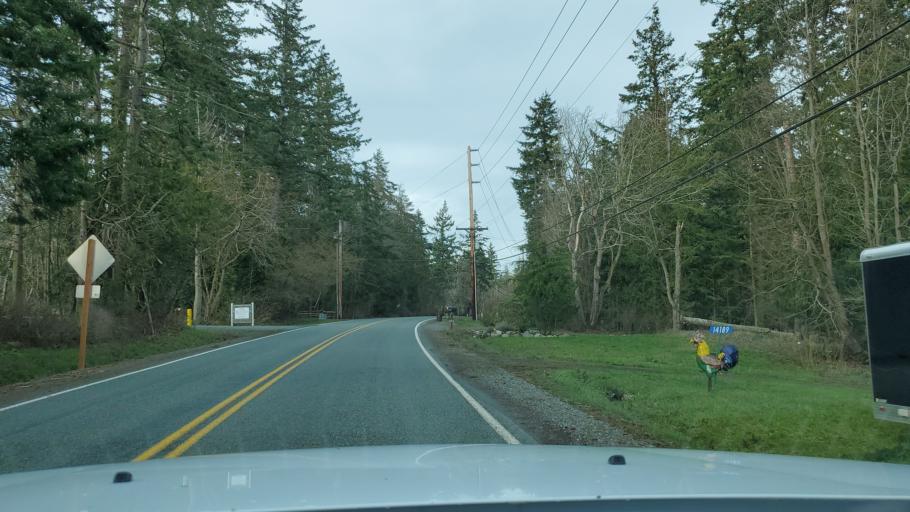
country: US
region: Washington
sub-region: Skagit County
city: Anacortes
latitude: 48.4374
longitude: -122.5825
